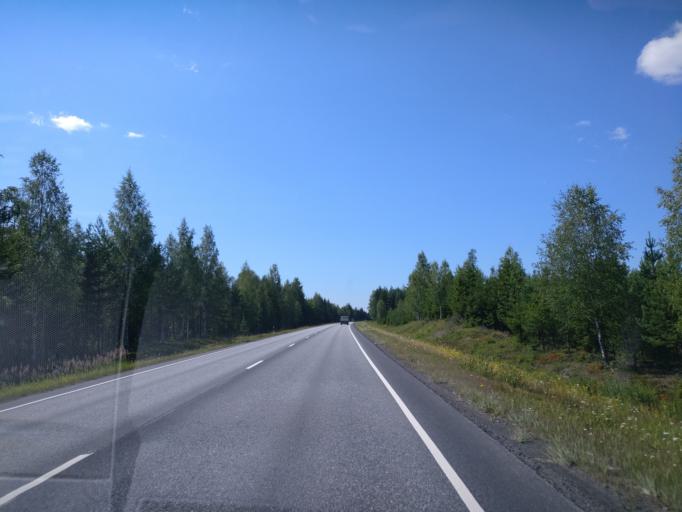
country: FI
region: Satakunta
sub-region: Pori
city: Kullaa
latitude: 61.4578
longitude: 22.0665
